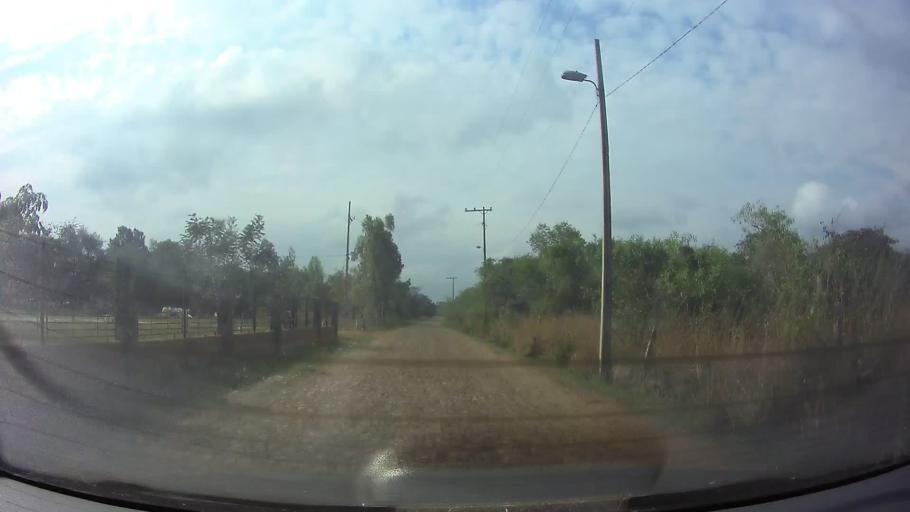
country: PY
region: Cordillera
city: Arroyos y Esteros
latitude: -24.9955
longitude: -57.1939
